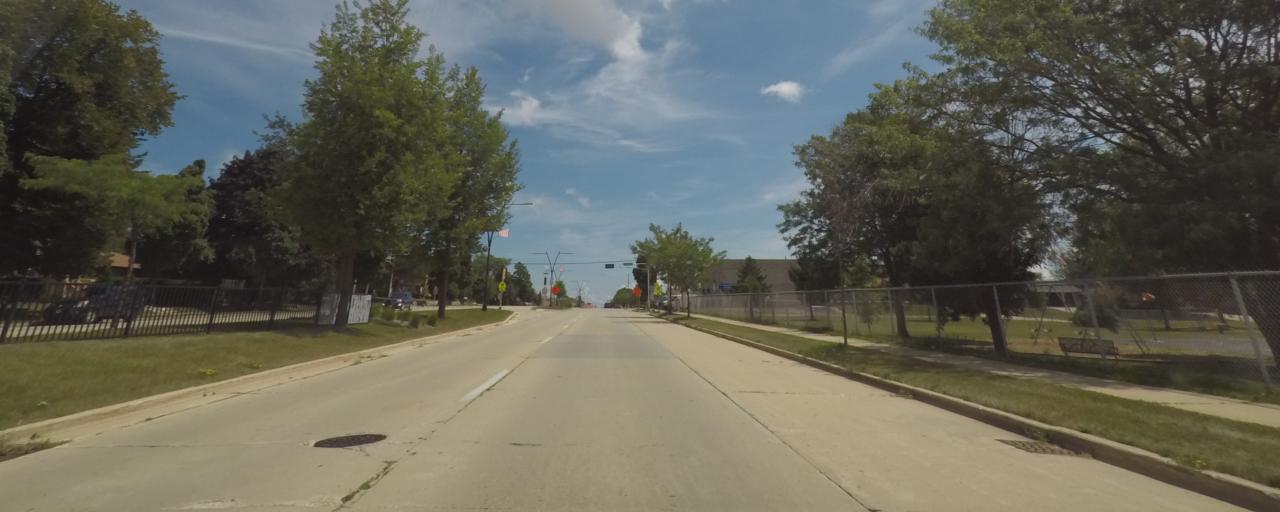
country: US
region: Wisconsin
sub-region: Milwaukee County
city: Greendale
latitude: 42.9593
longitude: -87.9746
